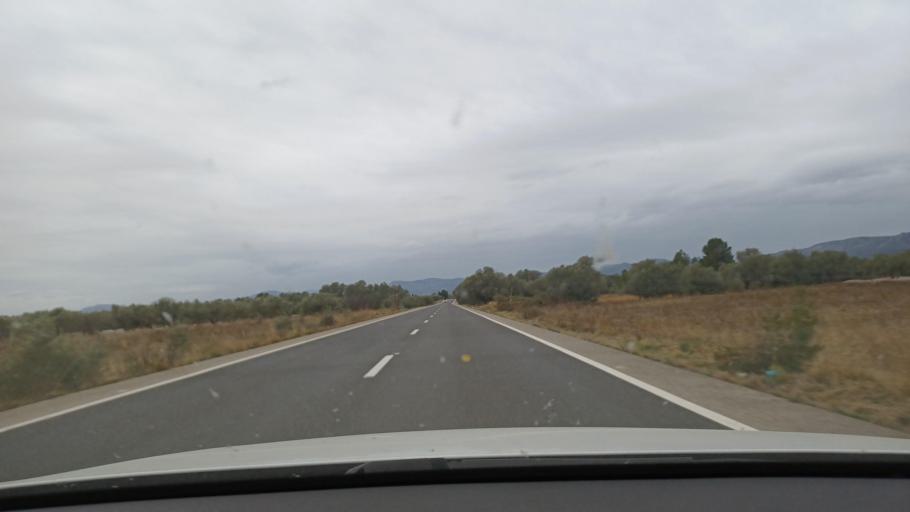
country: ES
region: Catalonia
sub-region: Provincia de Tarragona
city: Ulldecona
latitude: 40.6420
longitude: 0.3679
